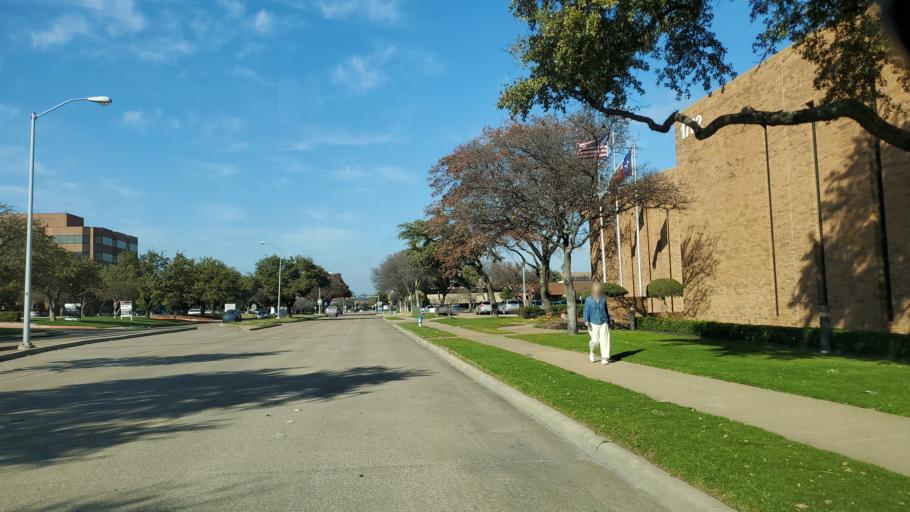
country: US
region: Texas
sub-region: Dallas County
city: Richardson
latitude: 32.9715
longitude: -96.7235
